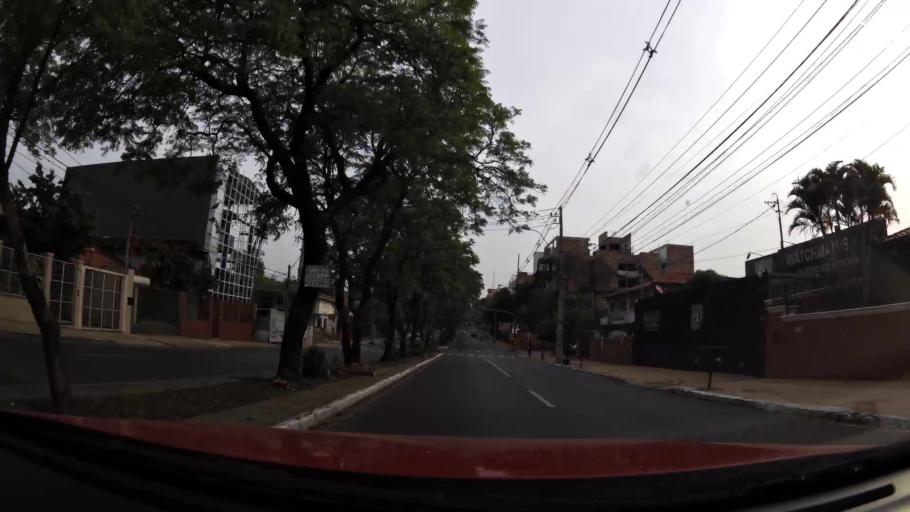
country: PY
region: Asuncion
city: Asuncion
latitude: -25.3017
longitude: -57.6063
